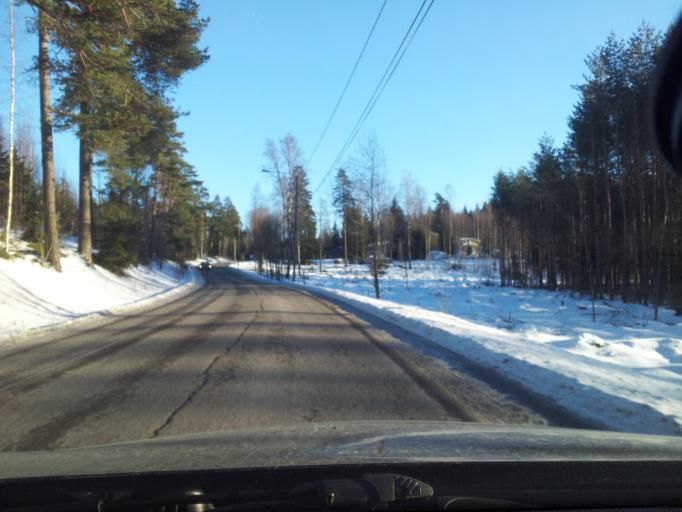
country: FI
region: Uusimaa
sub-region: Helsinki
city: Vihti
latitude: 60.3749
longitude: 24.3639
